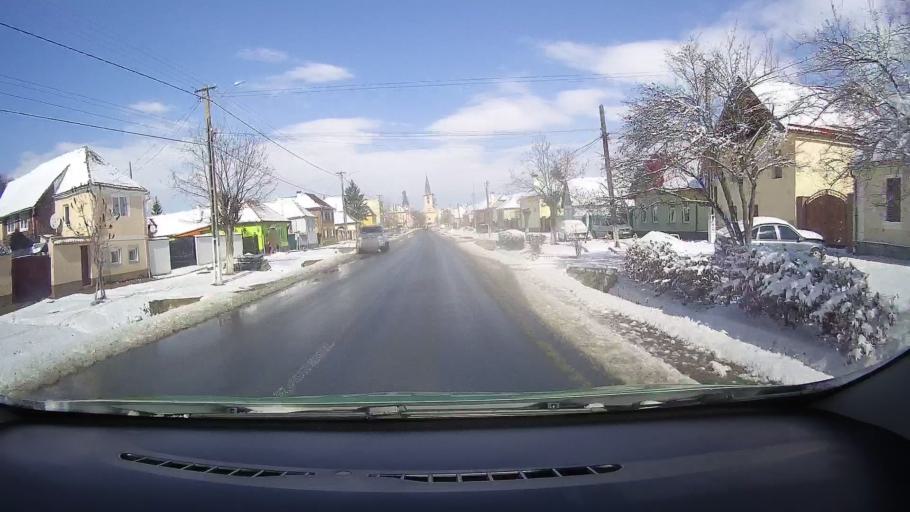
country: RO
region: Sibiu
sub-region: Comuna Nocrich
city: Nocrich
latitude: 45.8922
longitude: 24.4536
